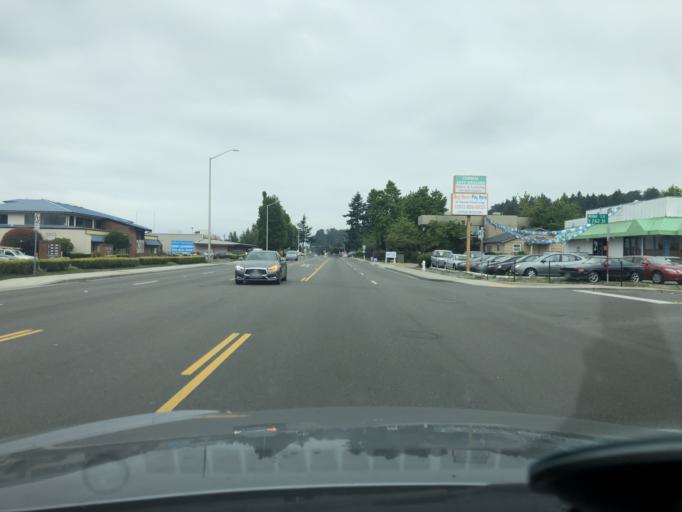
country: US
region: Washington
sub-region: King County
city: Kent
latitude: 47.3672
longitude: -122.2299
